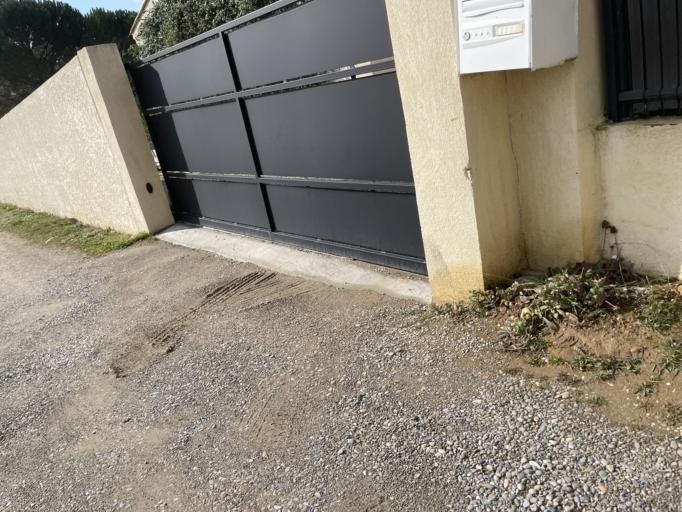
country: FR
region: Provence-Alpes-Cote d'Azur
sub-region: Departement du Var
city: Vinon-sur-Verdon
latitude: 43.7330
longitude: 5.8157
